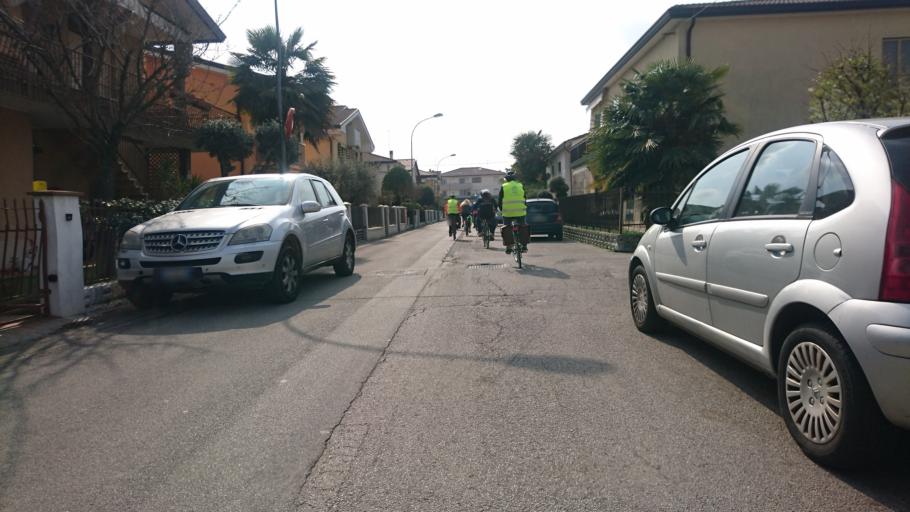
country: IT
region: Veneto
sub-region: Provincia di Padova
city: Abano Terme
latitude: 45.3557
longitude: 11.7657
